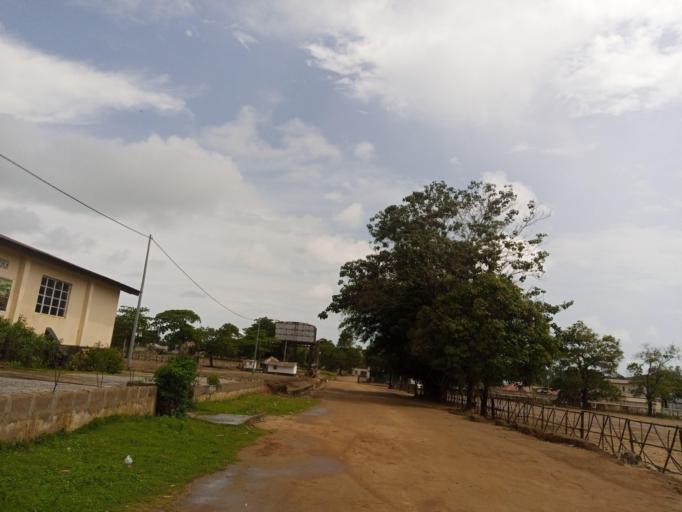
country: SL
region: Northern Province
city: Sawkta
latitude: 8.6275
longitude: -13.2067
